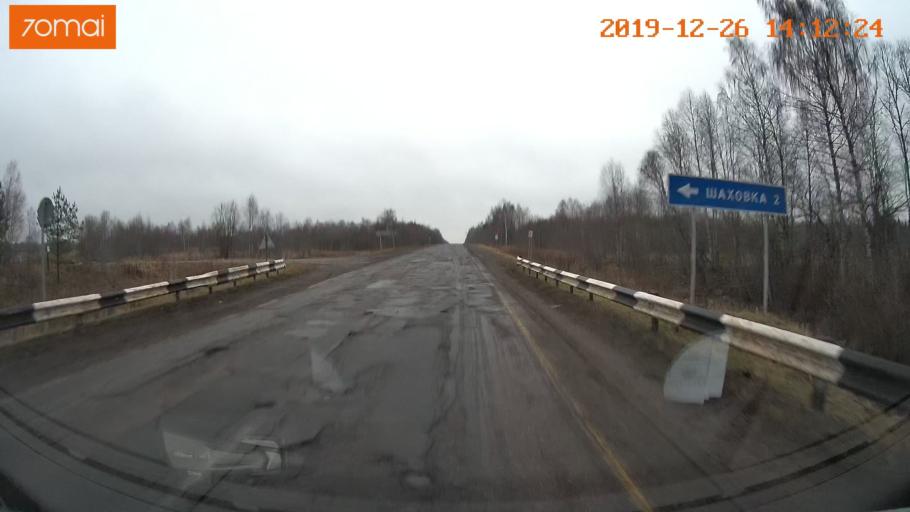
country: RU
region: Jaroslavl
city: Poshekhon'ye
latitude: 58.5110
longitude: 38.9896
